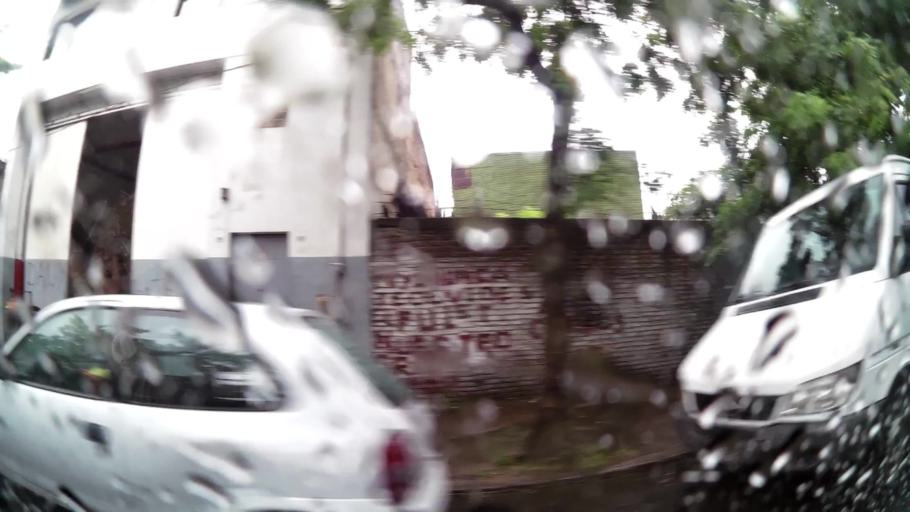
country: AR
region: Buenos Aires
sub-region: Partido de Avellaneda
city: Avellaneda
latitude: -34.6446
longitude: -58.3620
